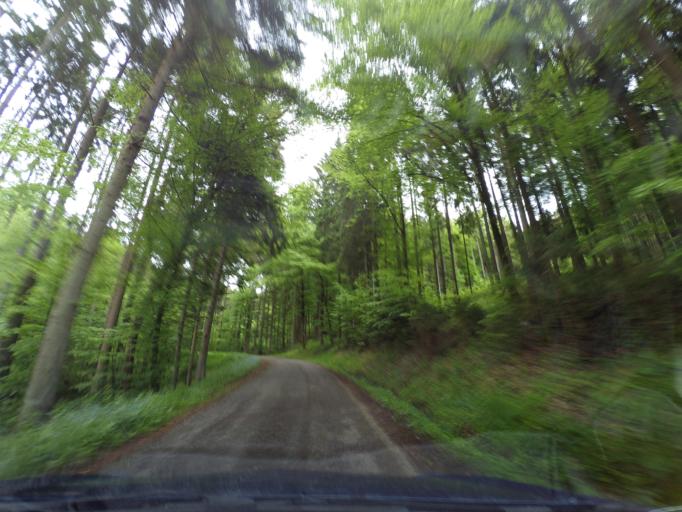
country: DE
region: Baden-Wuerttemberg
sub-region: Regierungsbezirk Stuttgart
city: Murrhardt
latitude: 48.9976
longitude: 9.5586
